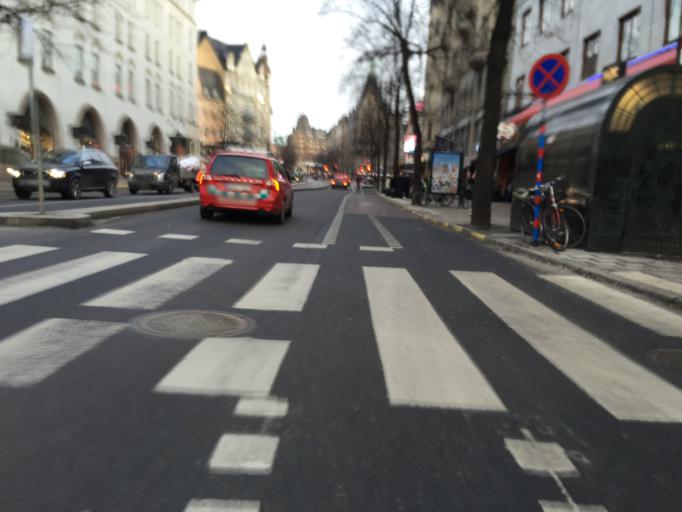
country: SE
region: Stockholm
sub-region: Stockholms Kommun
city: Stockholm
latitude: 59.3349
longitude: 18.0740
